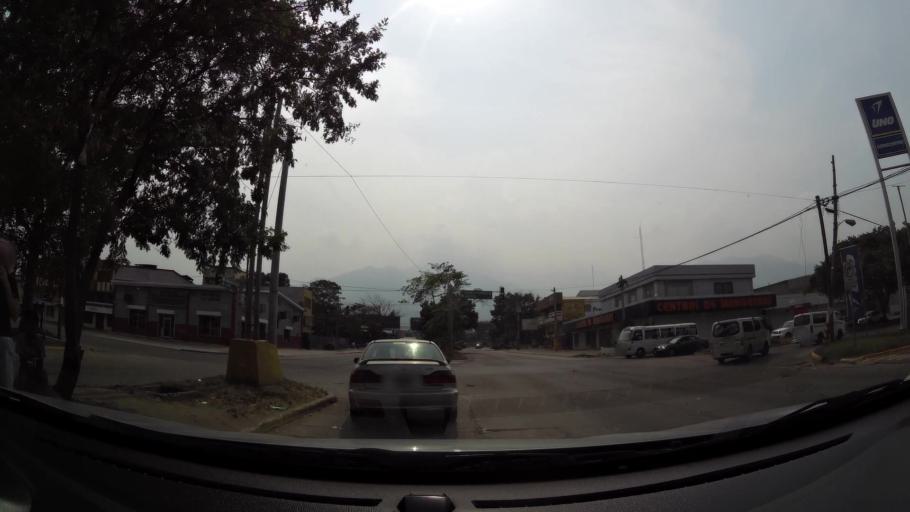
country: HN
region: Cortes
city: San Pedro Sula
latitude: 15.5180
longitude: -88.0232
